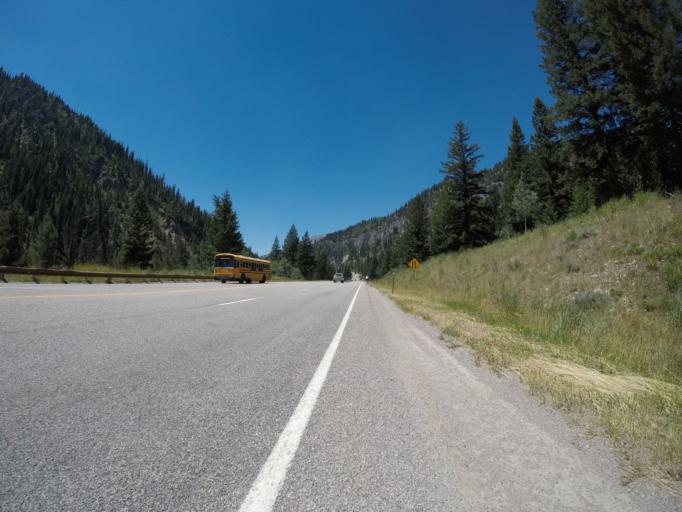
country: US
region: Wyoming
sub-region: Teton County
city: Hoback
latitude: 43.1979
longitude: -110.8976
